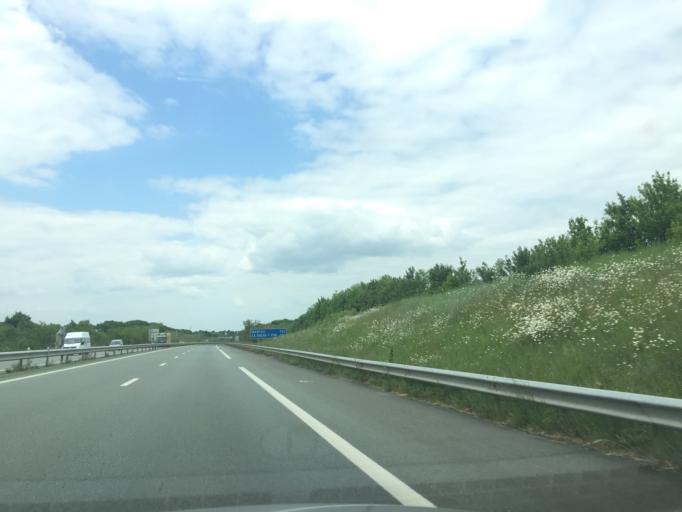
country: FR
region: Poitou-Charentes
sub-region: Departement des Deux-Sevres
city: Chauray
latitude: 46.3635
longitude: -0.3476
